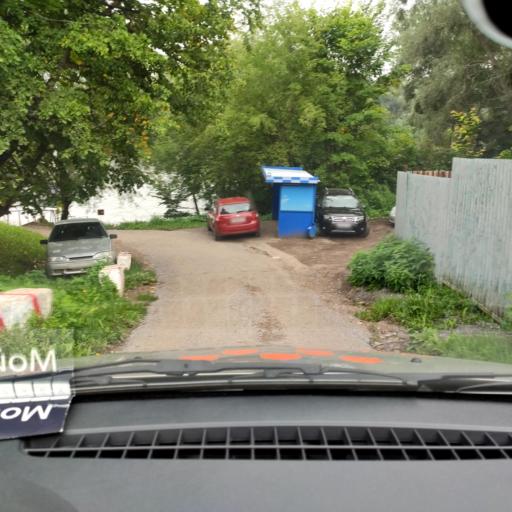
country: RU
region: Bashkortostan
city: Ufa
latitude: 54.7246
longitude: 56.0294
